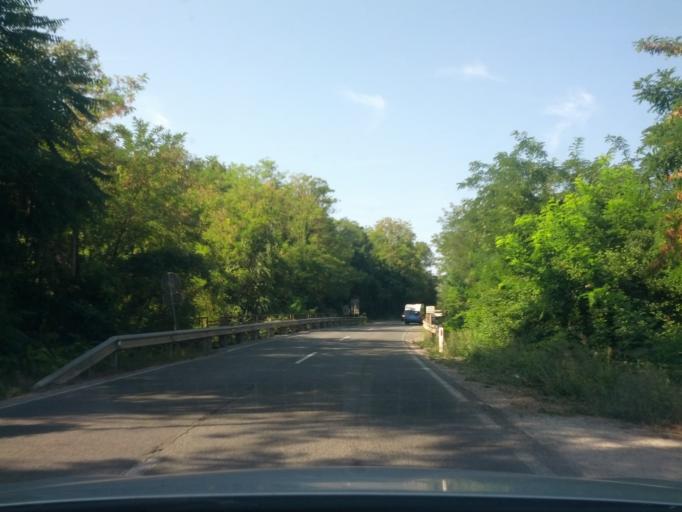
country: SI
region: Izola-Isola
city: Izola
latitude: 45.4952
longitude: 13.6777
